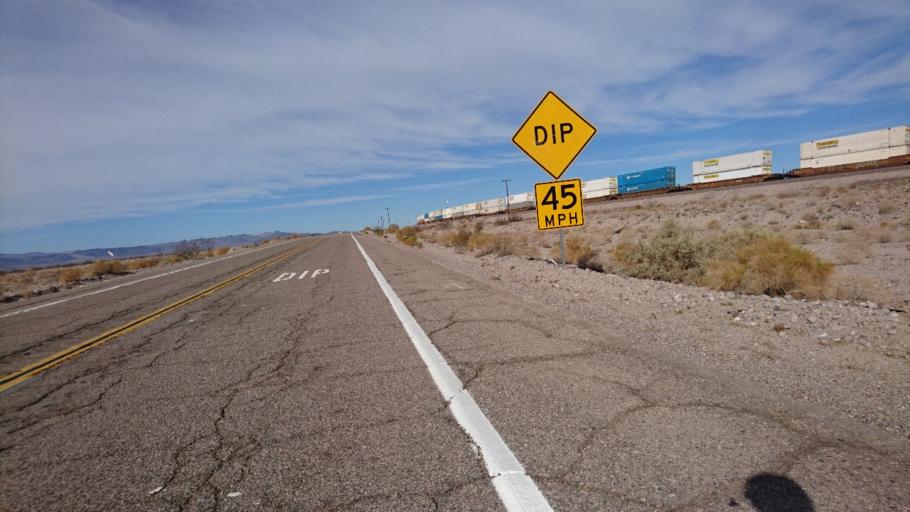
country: US
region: California
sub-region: San Bernardino County
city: Twentynine Palms
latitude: 34.6020
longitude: -115.9530
